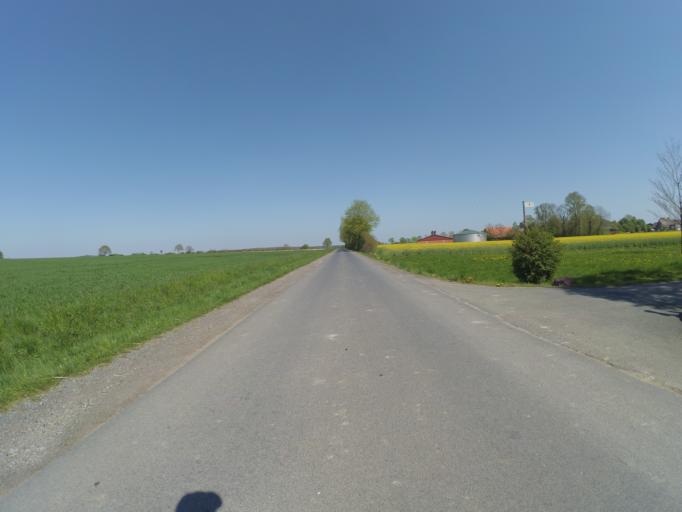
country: DE
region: North Rhine-Westphalia
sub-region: Regierungsbezirk Munster
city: Ascheberg
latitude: 51.7836
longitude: 7.5775
